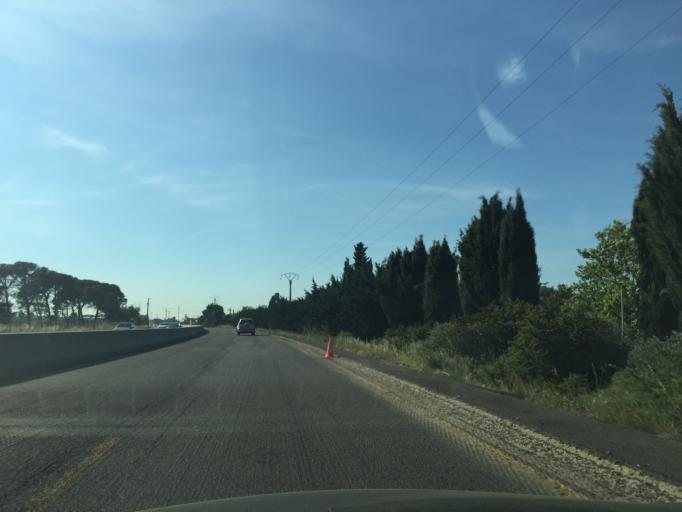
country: FR
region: Provence-Alpes-Cote d'Azur
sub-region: Departement des Bouches-du-Rhone
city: Fos-sur-Mer
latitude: 43.4691
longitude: 4.9116
